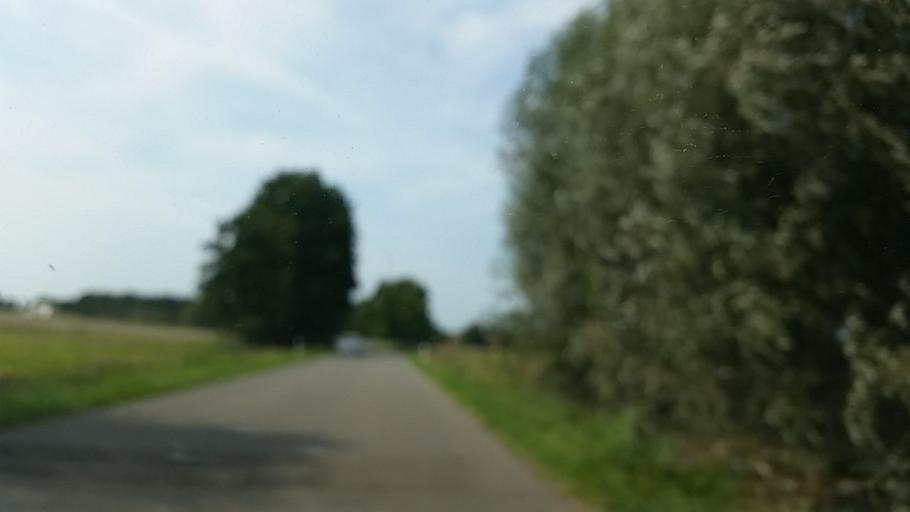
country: DE
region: Saxony-Anhalt
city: Salzwedel
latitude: 52.8440
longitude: 11.1323
